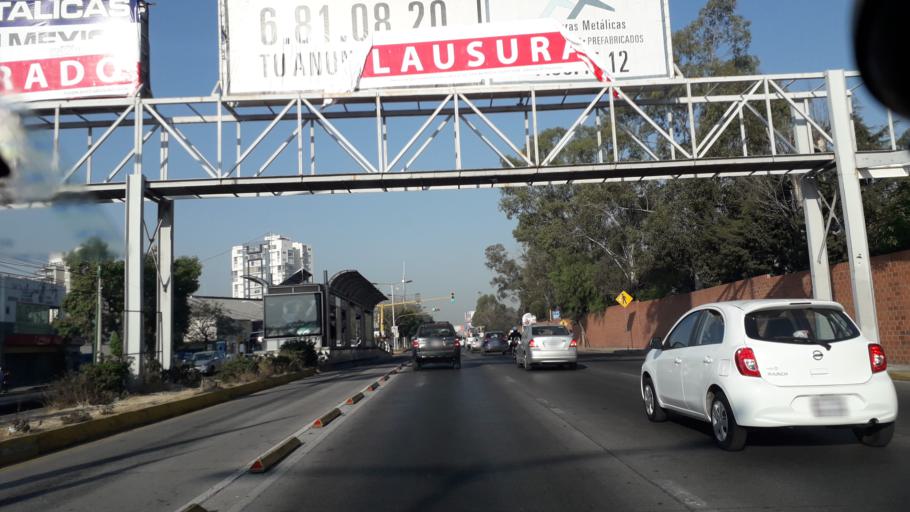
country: MX
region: Puebla
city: Puebla
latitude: 19.0395
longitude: -98.2413
